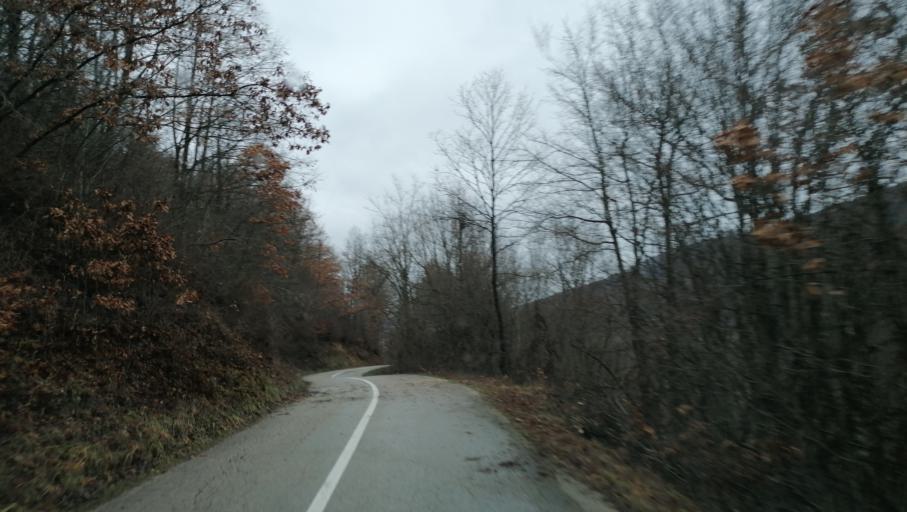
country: RS
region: Central Serbia
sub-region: Pirotski Okrug
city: Dimitrovgrad
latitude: 42.9833
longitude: 22.7827
